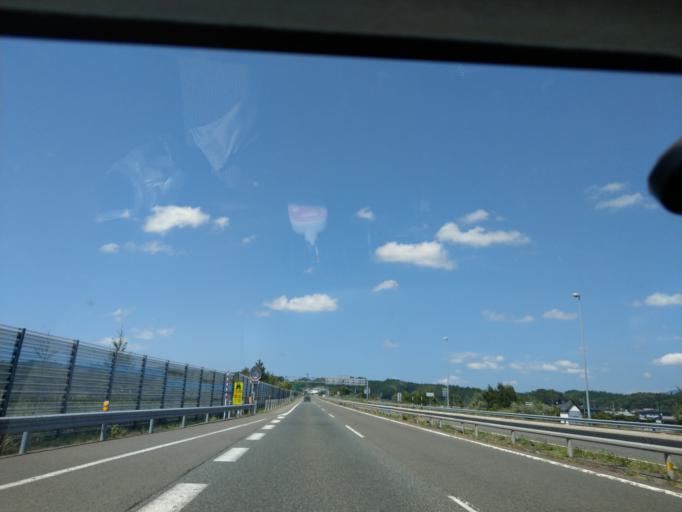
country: JP
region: Akita
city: Akita
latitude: 39.6444
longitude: 140.2091
